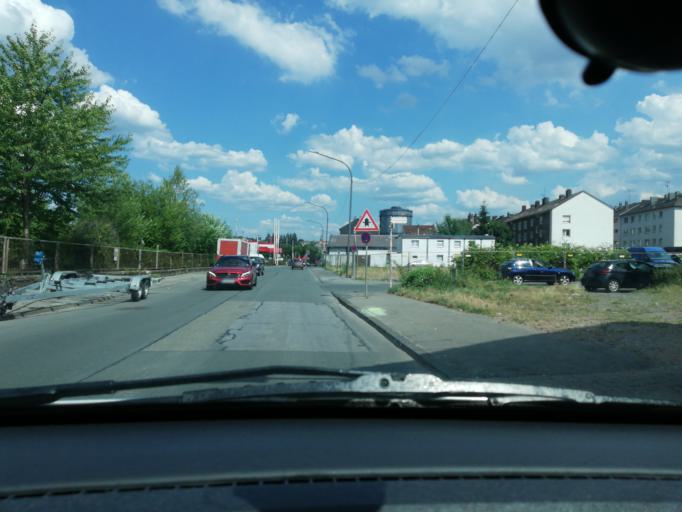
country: DE
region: North Rhine-Westphalia
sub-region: Regierungsbezirk Dusseldorf
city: Wuppertal
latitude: 51.2726
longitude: 7.2170
